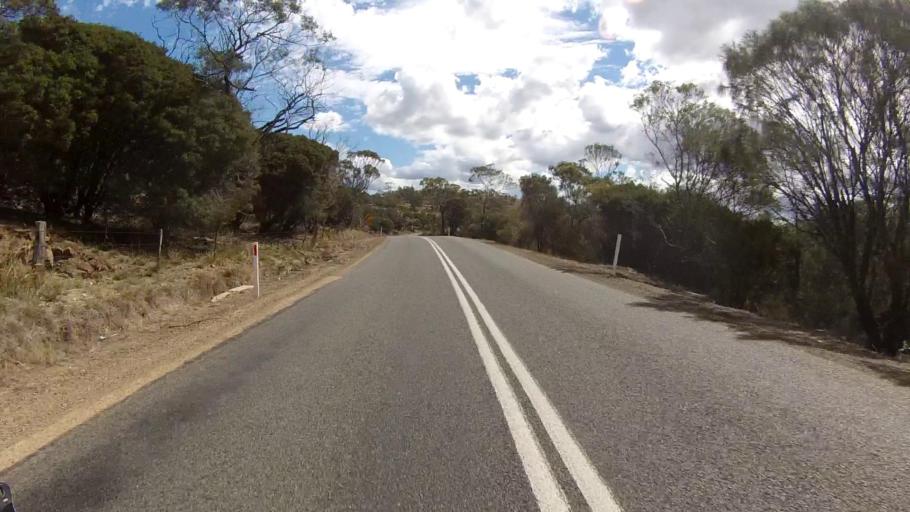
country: AU
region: Tasmania
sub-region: Break O'Day
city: St Helens
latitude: -41.9939
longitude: 148.1090
